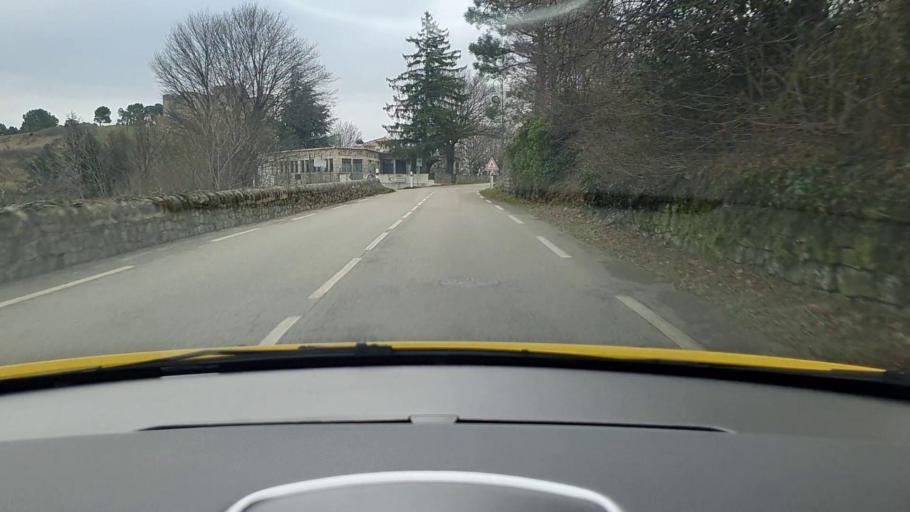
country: FR
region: Languedoc-Roussillon
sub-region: Departement du Gard
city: Branoux-les-Taillades
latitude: 44.2690
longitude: 4.0239
